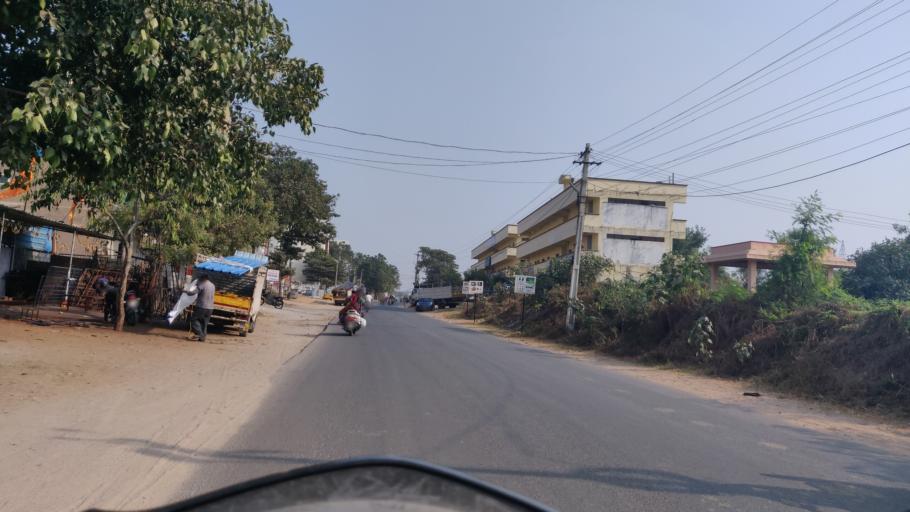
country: IN
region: Telangana
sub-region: Rangareddi
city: Uppal Kalan
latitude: 17.3990
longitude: 78.5856
